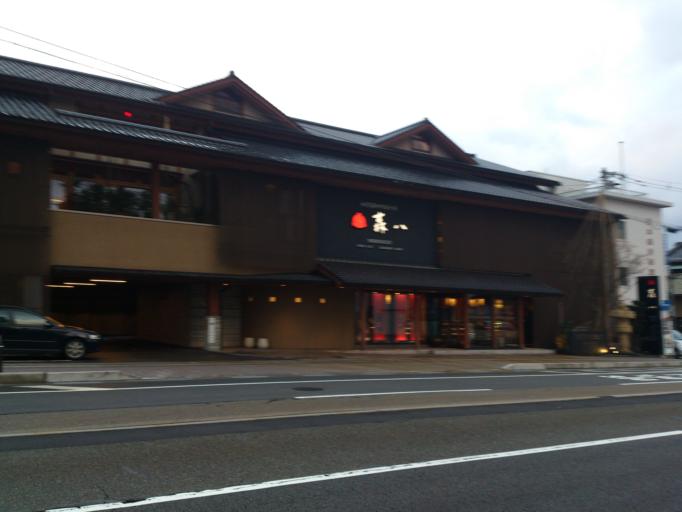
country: JP
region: Ishikawa
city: Kanazawa-shi
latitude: 36.5693
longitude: 136.6643
